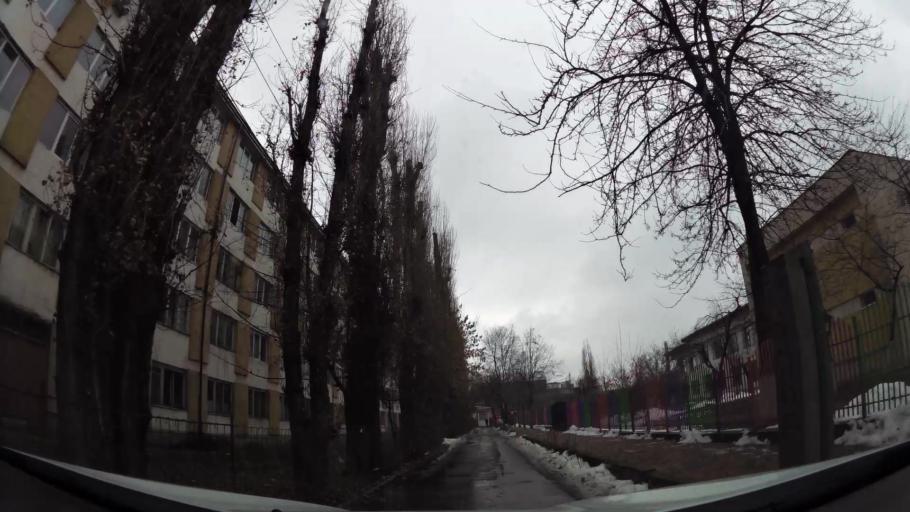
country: RO
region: Ilfov
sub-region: Comuna Popesti-Leordeni
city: Popesti-Leordeni
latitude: 44.4091
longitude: 26.1432
